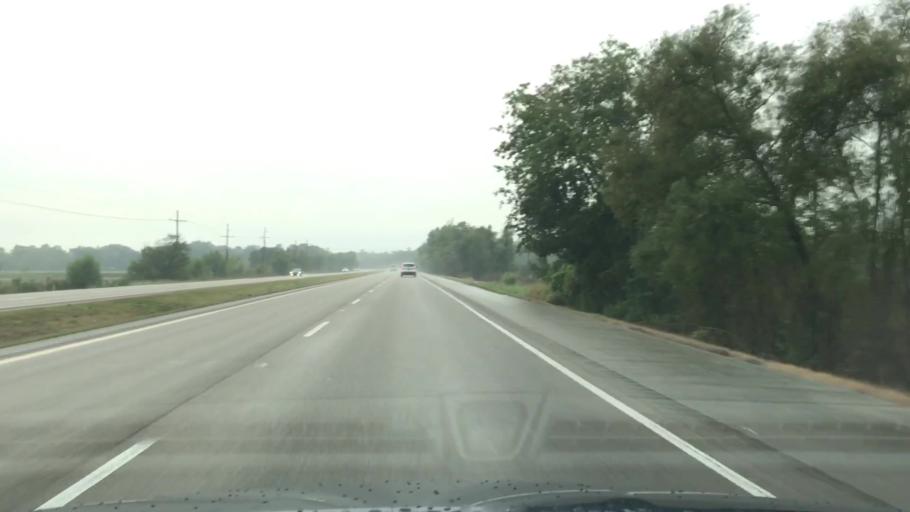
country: US
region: Louisiana
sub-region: Saint Charles Parish
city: Paradis
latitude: 29.8608
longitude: -90.4465
